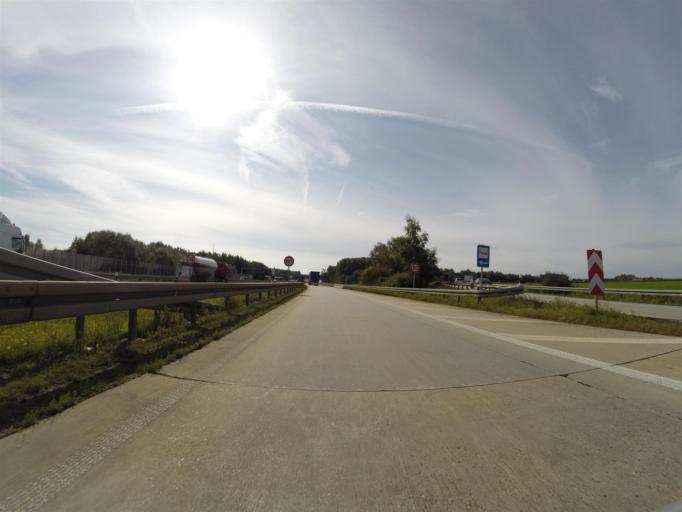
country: DE
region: Thuringia
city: Hermsdorf
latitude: 50.8833
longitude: 11.8459
